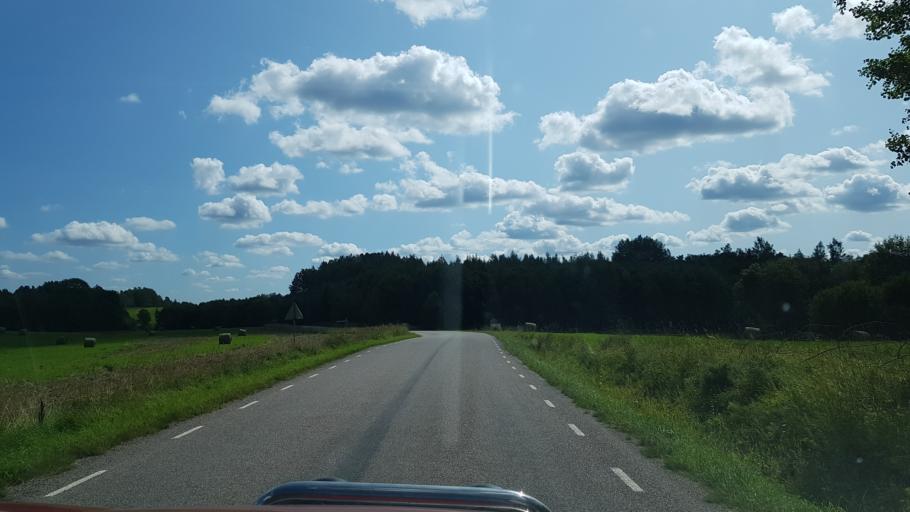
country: EE
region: Vorumaa
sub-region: Voru linn
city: Voru
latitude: 57.6706
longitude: 27.0820
